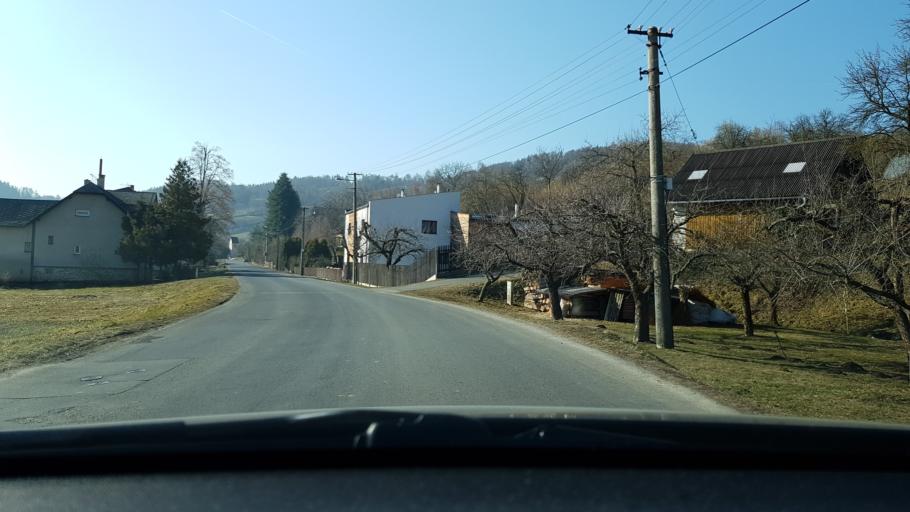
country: CZ
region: Olomoucky
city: Olsany
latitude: 49.9685
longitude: 16.8607
